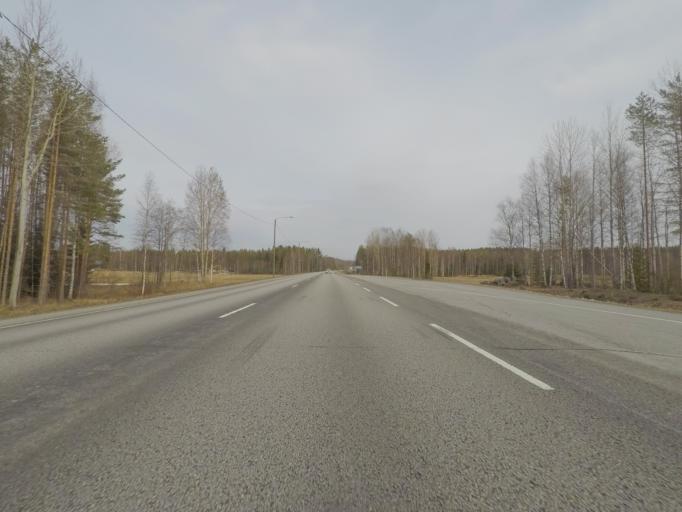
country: FI
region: Central Finland
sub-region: Jyvaeskylae
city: Hankasalmi
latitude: 62.2549
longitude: 26.2613
